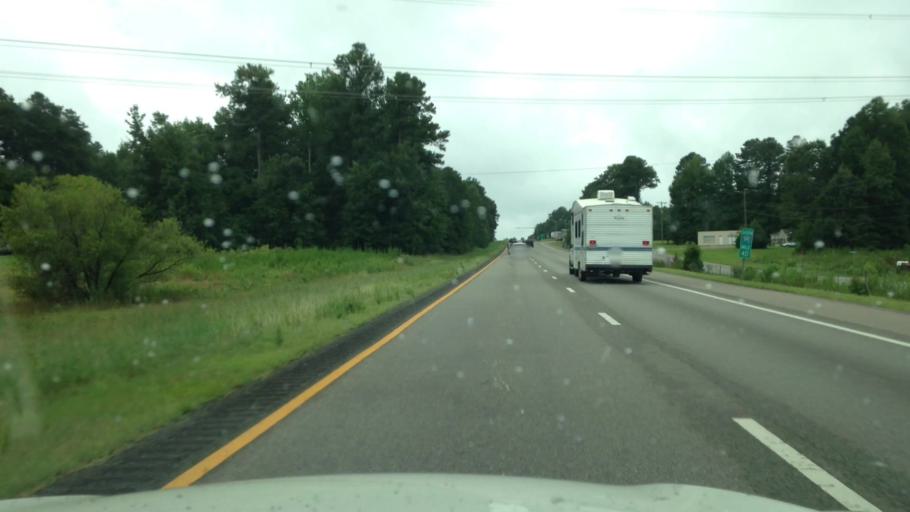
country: US
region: Virginia
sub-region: City of Petersburg
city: Petersburg
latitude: 37.0691
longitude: -77.3691
